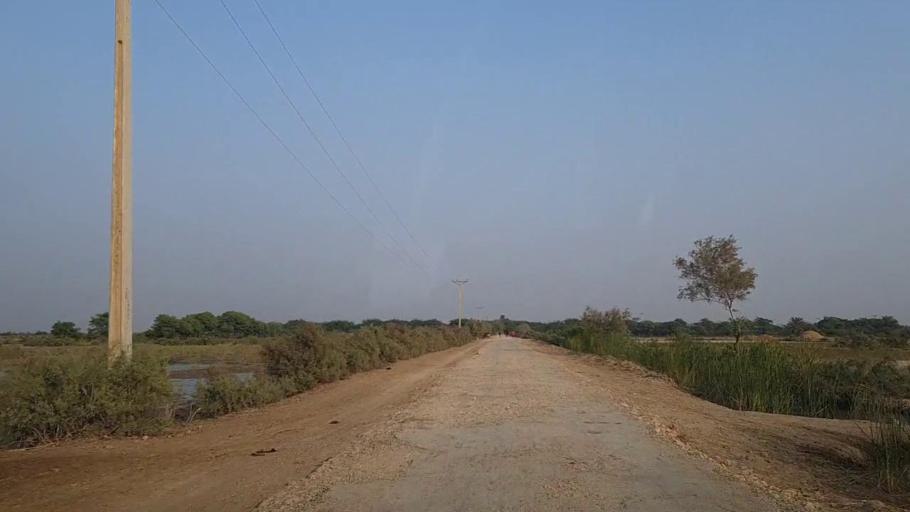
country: PK
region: Sindh
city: Thatta
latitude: 24.6921
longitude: 67.8062
